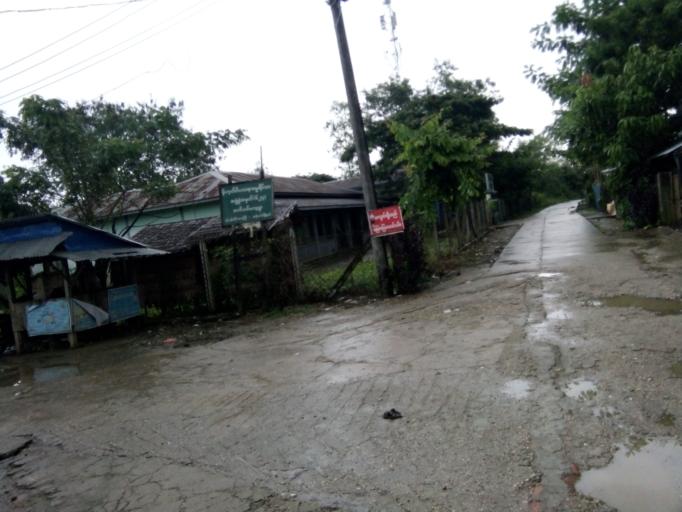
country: MM
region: Yangon
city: Kanbe
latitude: 16.8740
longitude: 95.9828
